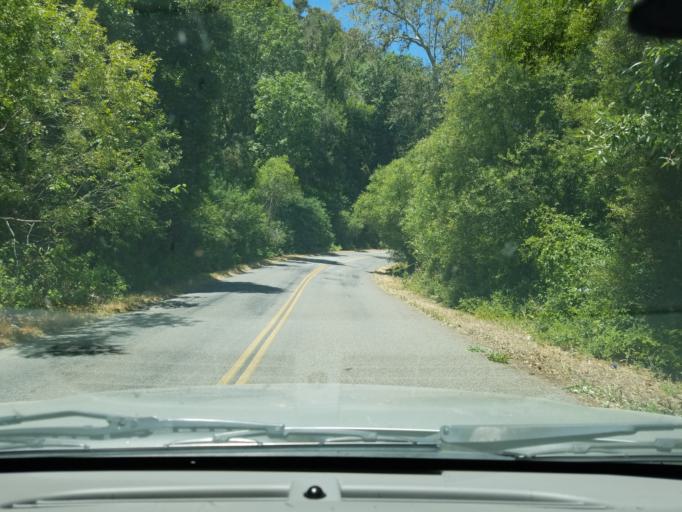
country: US
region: California
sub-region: Monterey County
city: Carmel Valley Village
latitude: 36.4444
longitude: -121.6771
